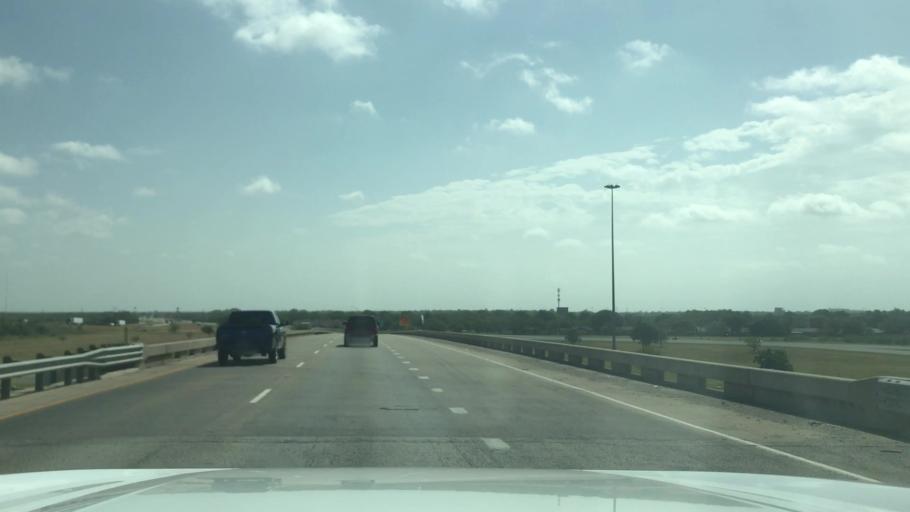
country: US
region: Texas
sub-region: Taylor County
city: Abilene
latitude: 32.4819
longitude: -99.7710
